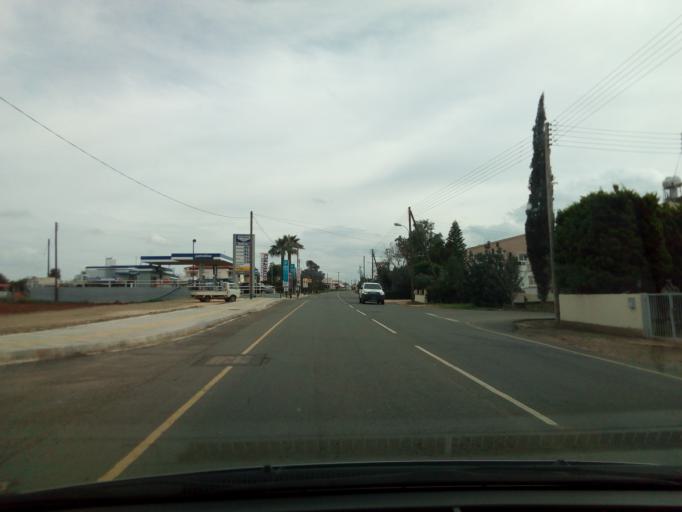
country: CY
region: Lefkosia
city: Astromeritis
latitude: 35.1382
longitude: 33.0528
